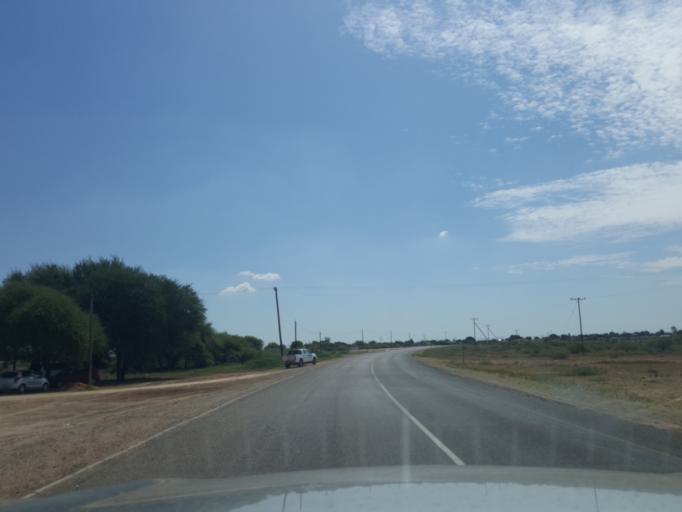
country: BW
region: Kweneng
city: Letlhakeng
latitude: -24.1167
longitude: 25.0423
